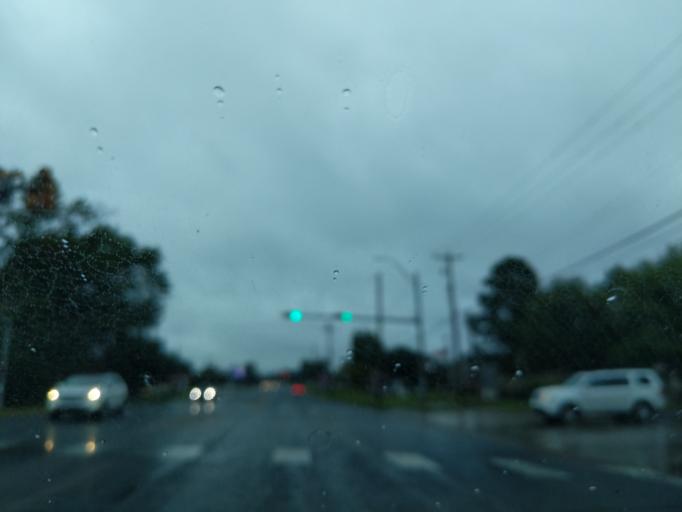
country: US
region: Texas
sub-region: Nacogdoches County
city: Nacogdoches
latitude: 31.6496
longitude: -94.6554
